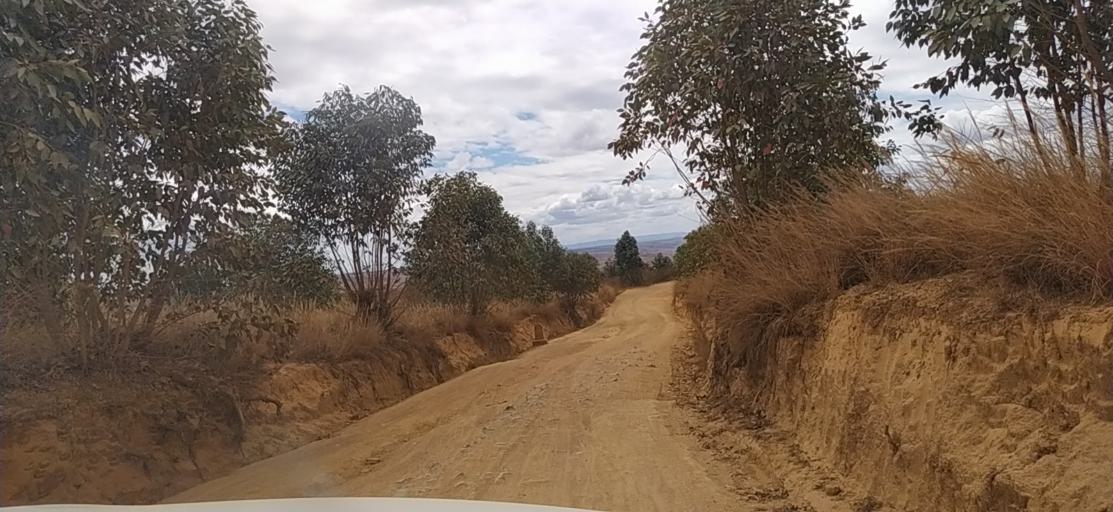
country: MG
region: Alaotra Mangoro
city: Ambatondrazaka
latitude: -17.9910
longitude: 48.2642
